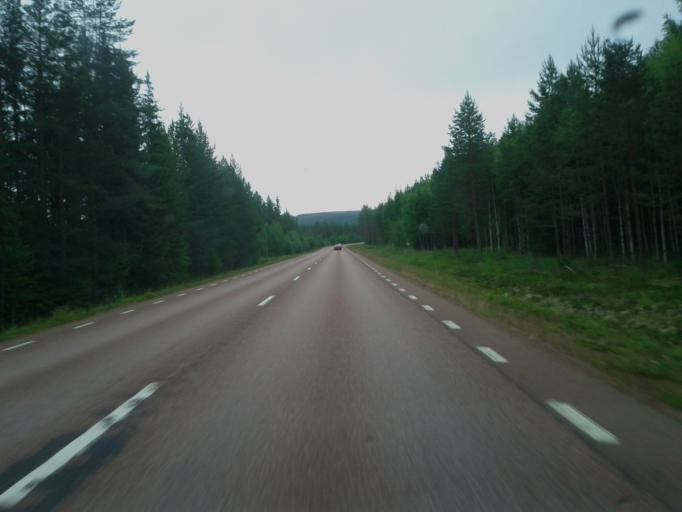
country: SE
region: Dalarna
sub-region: Alvdalens Kommun
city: AElvdalen
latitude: 61.2756
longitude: 13.7811
